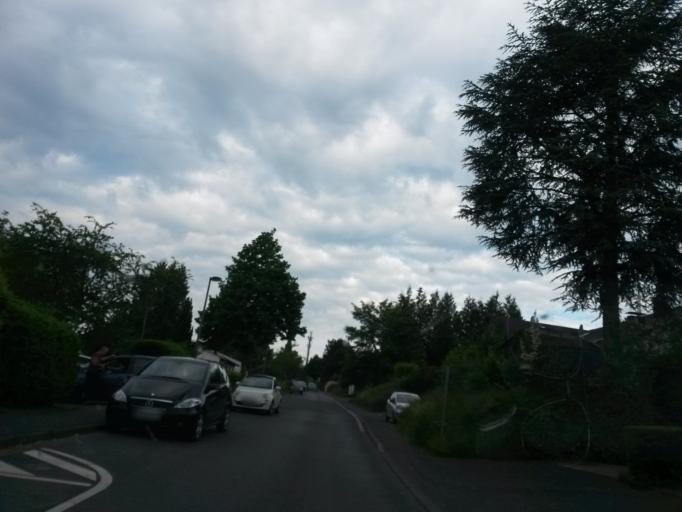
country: DE
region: North Rhine-Westphalia
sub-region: Regierungsbezirk Koln
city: Overath
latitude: 50.9071
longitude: 7.2416
